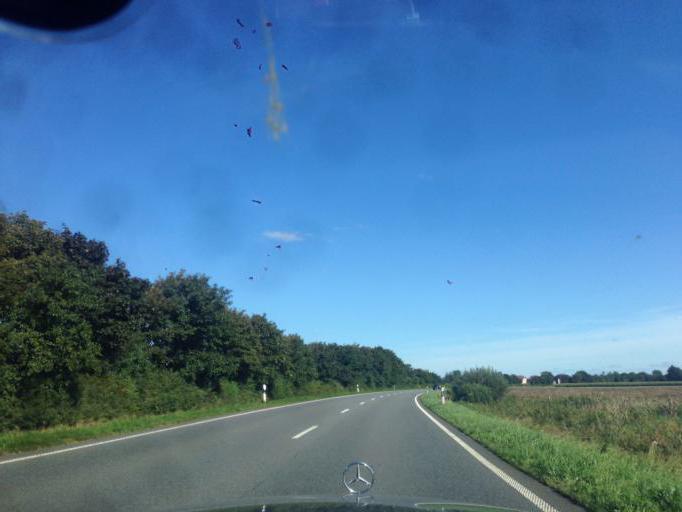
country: DE
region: Schleswig-Holstein
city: Horup
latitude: 54.7493
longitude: 9.0835
